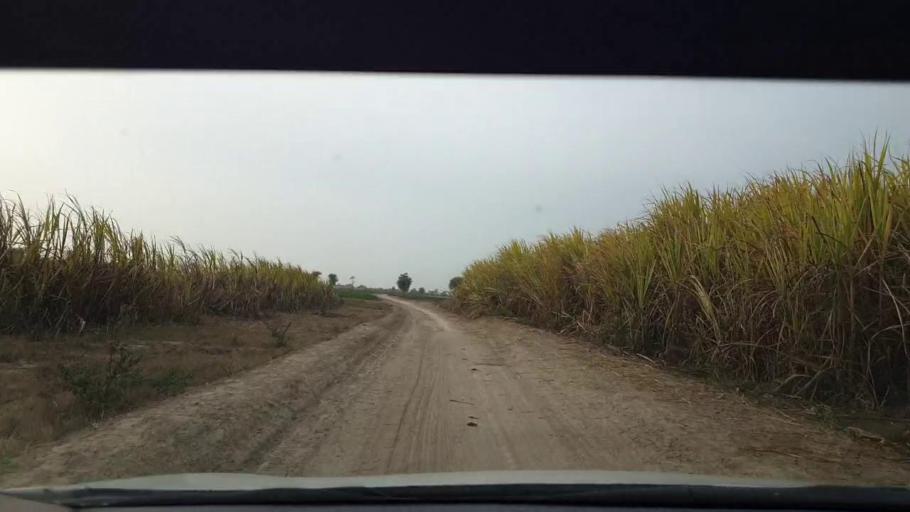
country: PK
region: Sindh
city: Jhol
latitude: 25.9061
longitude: 68.7897
